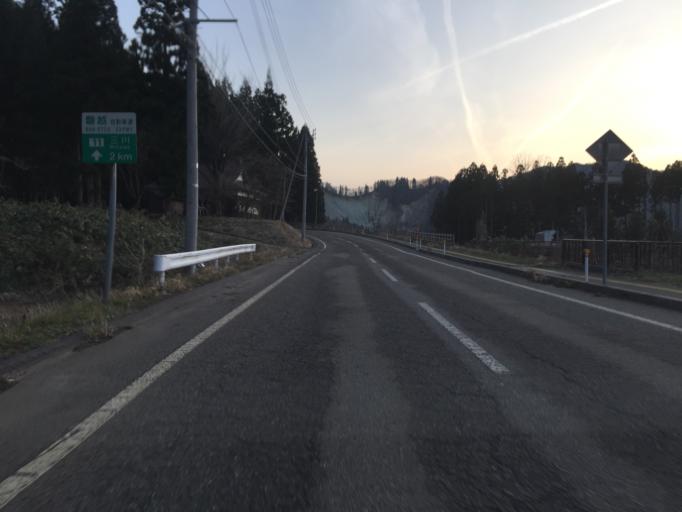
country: JP
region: Niigata
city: Suibara
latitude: 37.7152
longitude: 139.3709
